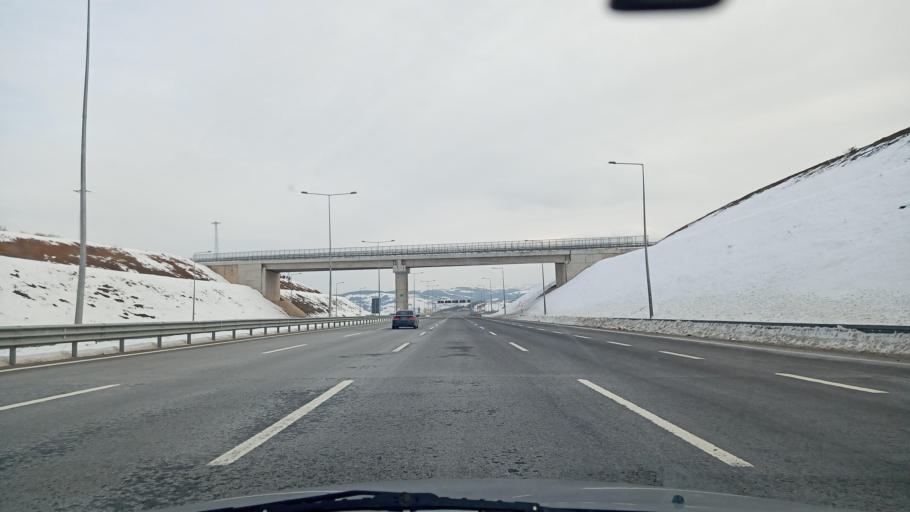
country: TR
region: Kocaeli
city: Korfez
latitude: 40.8894
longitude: 29.7224
